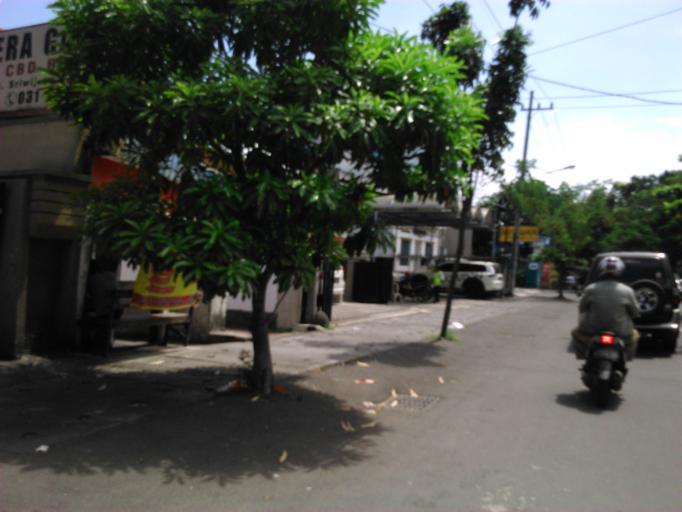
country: ID
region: East Java
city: Gubengairlangga
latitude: -7.2801
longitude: 112.7420
